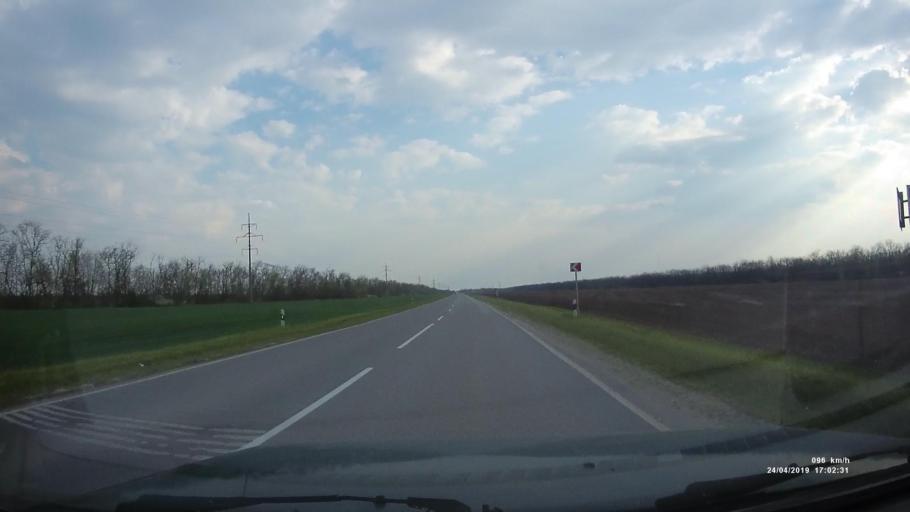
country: RU
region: Rostov
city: Sal'sk
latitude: 46.5794
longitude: 41.6150
